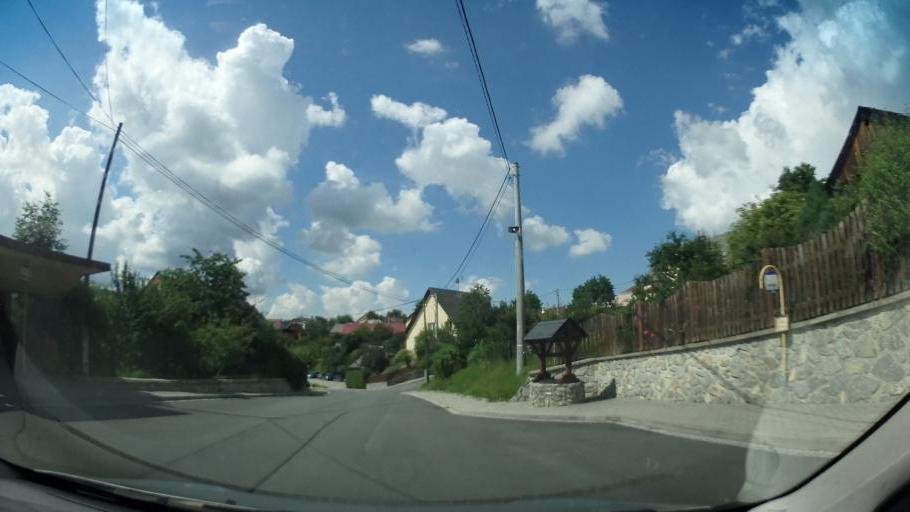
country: CZ
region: Olomoucky
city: Zabreh
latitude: 49.8757
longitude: 16.8470
